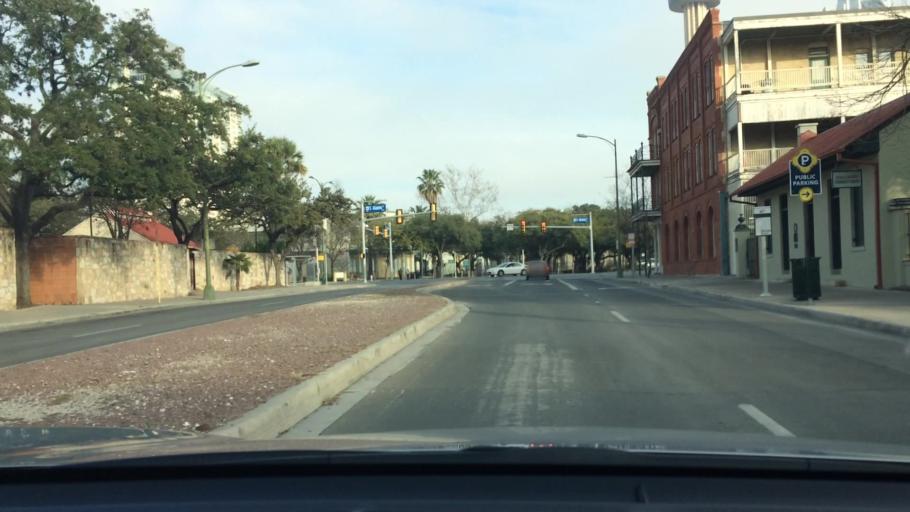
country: US
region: Texas
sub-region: Bexar County
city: San Antonio
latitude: 29.4209
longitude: -98.4890
